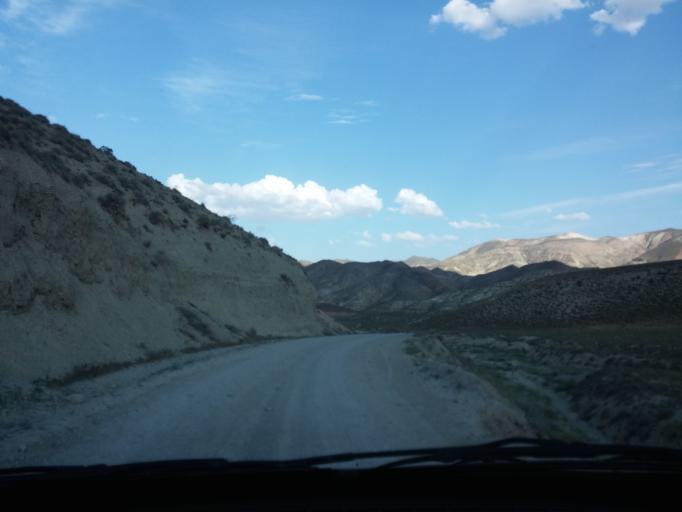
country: IR
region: Tehran
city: Damavand
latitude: 35.5332
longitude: 52.2335
